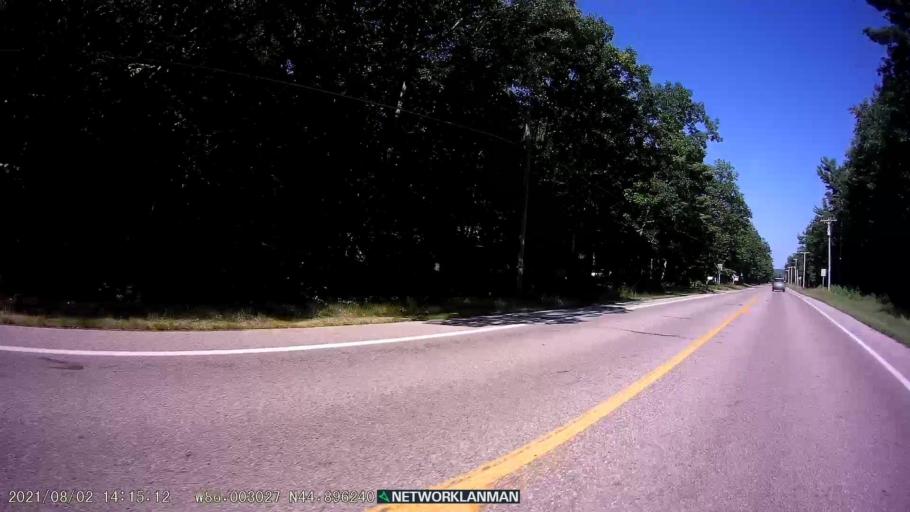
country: US
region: Michigan
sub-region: Leelanau County
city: Leland
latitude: 44.8963
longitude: -86.0027
